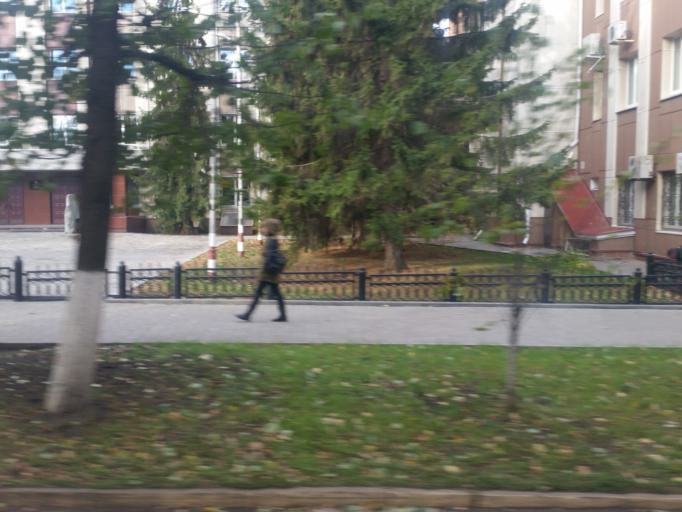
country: RU
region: Ulyanovsk
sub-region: Ulyanovskiy Rayon
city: Ulyanovsk
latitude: 54.3141
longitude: 48.3865
